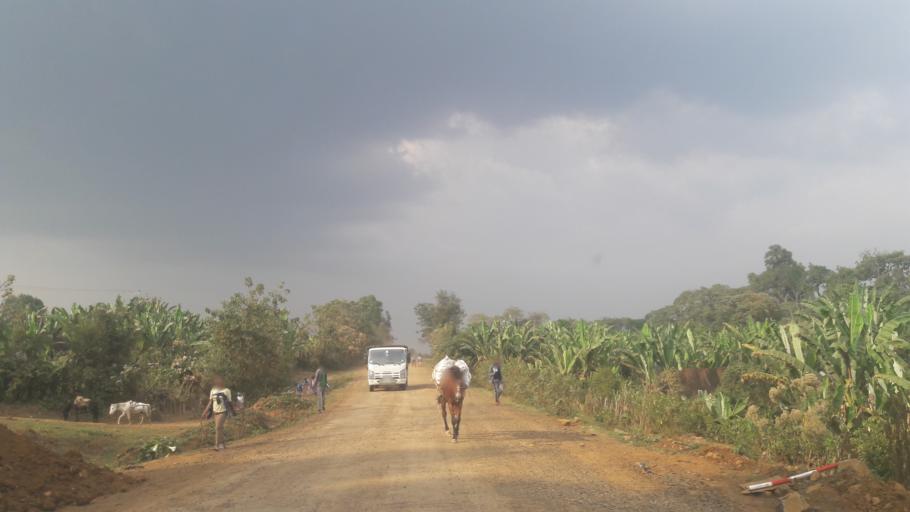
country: ET
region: Oromiya
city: Gore
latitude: 7.7260
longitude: 35.4831
